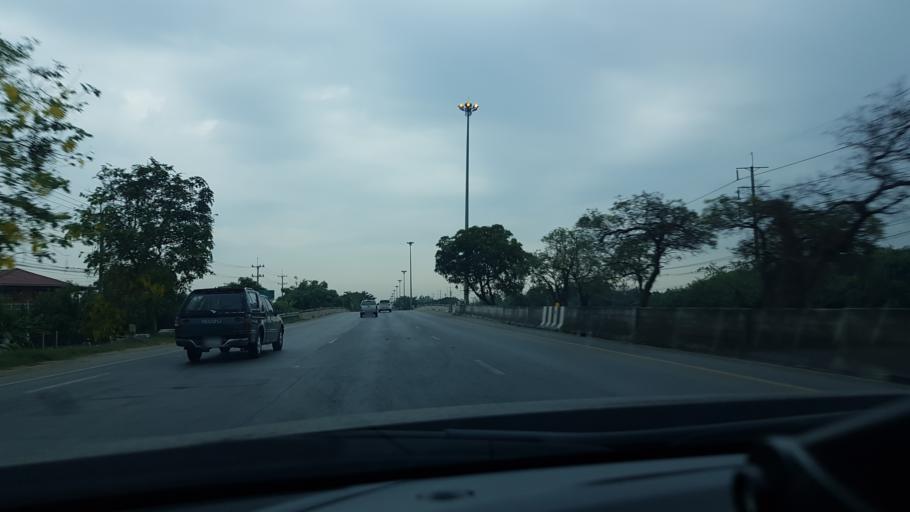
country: TH
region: Pathum Thani
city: Sam Khok
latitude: 14.0804
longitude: 100.5707
